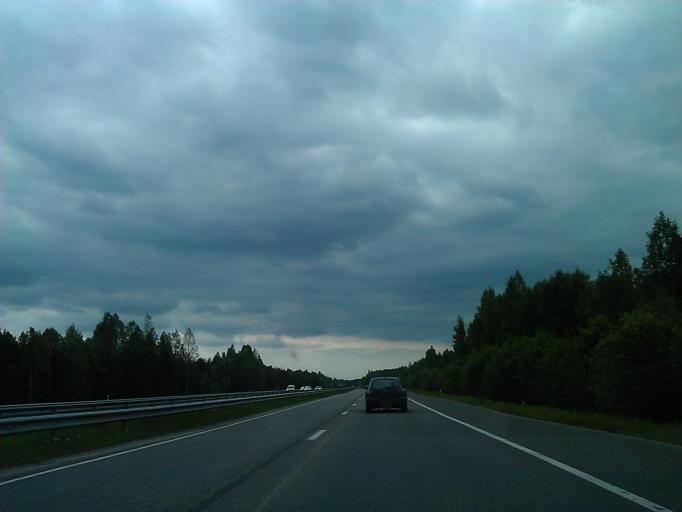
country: LV
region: Marupe
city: Marupe
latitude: 56.8670
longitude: 24.0660
